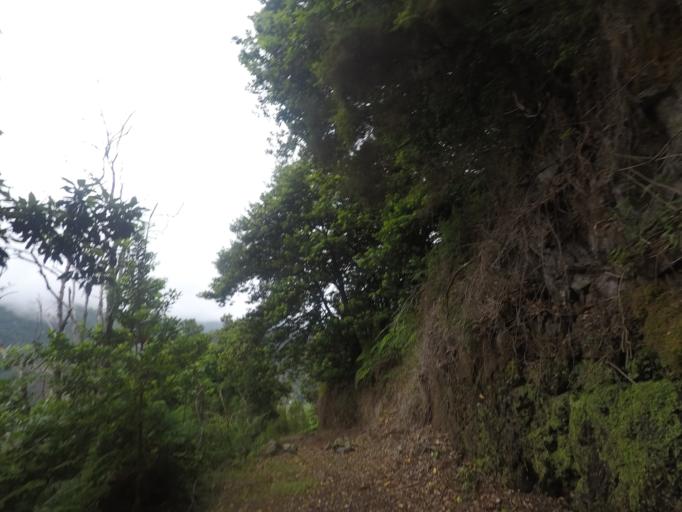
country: PT
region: Madeira
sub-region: Santana
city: Santana
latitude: 32.7542
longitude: -16.8746
